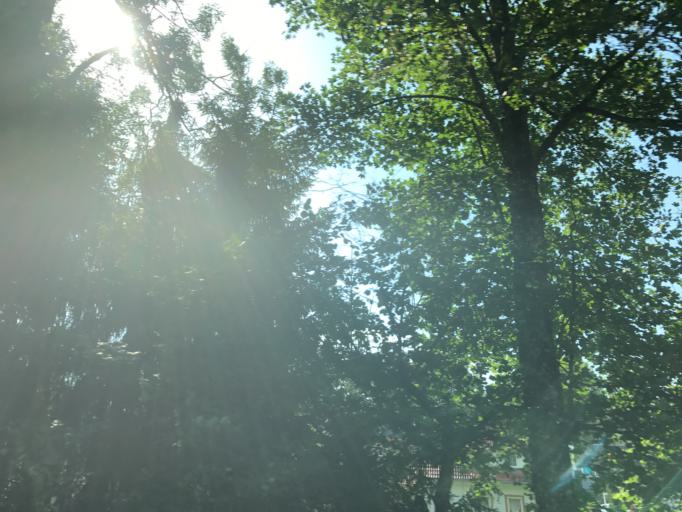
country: DE
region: Baden-Wuerttemberg
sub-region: Tuebingen Region
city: Wangen im Allgau
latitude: 47.7194
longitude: 9.8631
